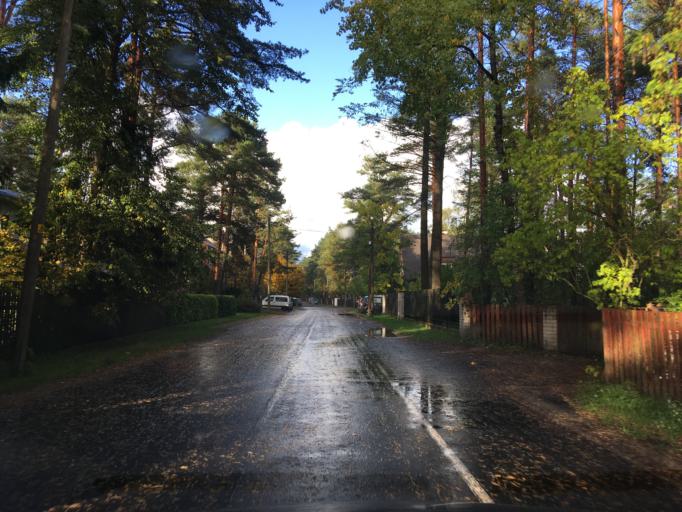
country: EE
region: Harju
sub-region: Tallinna linn
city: Tallinn
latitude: 59.3776
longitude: 24.7109
